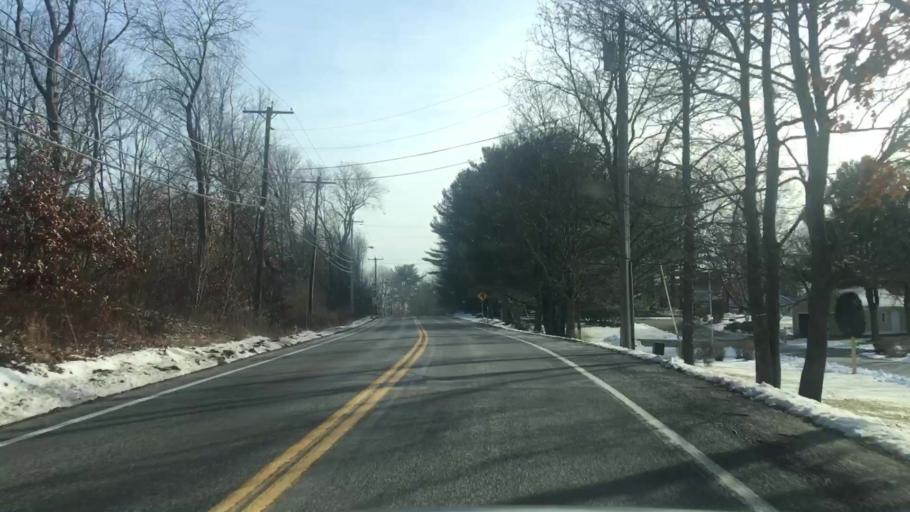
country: US
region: New Hampshire
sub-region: Merrimack County
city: East Concord
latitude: 43.2594
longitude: -71.5462
